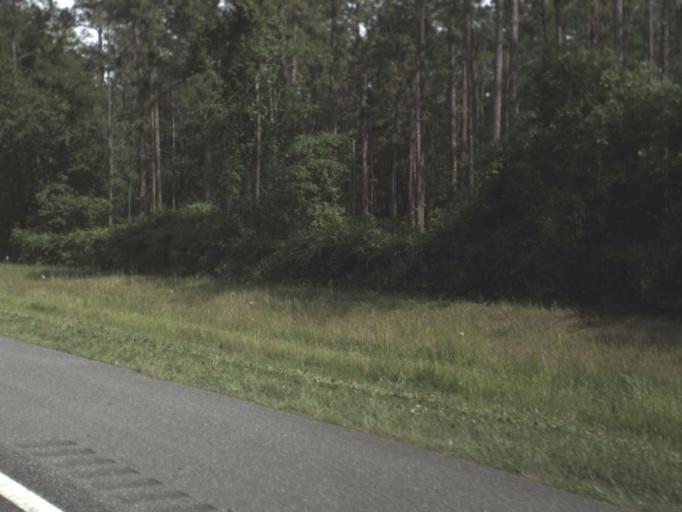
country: US
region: Florida
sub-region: Columbia County
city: Five Points
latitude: 30.2411
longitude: -82.5980
